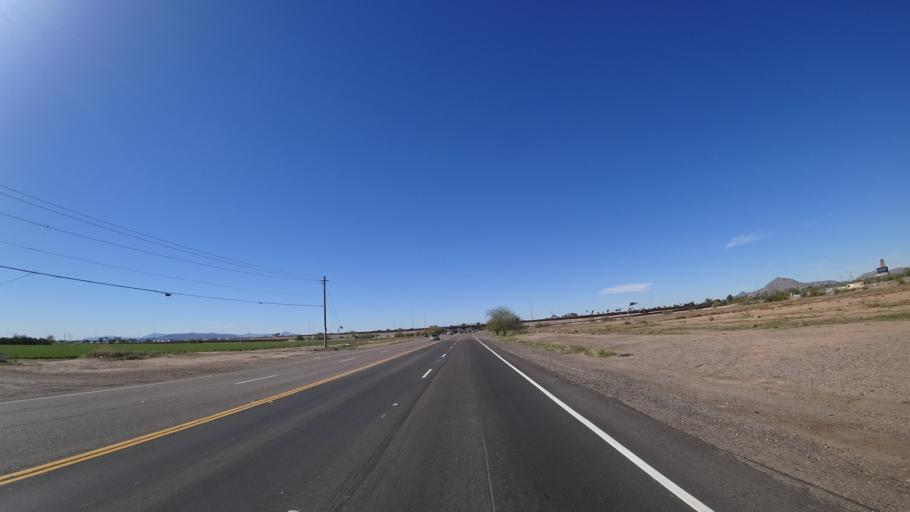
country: US
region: Arizona
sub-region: Maricopa County
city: Tempe
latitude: 33.4514
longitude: -111.8862
